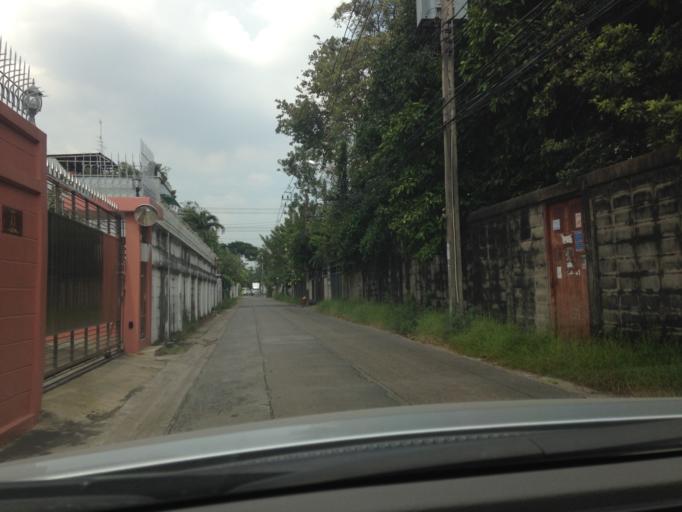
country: TH
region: Bangkok
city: Chatuchak
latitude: 13.8374
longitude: 100.5398
